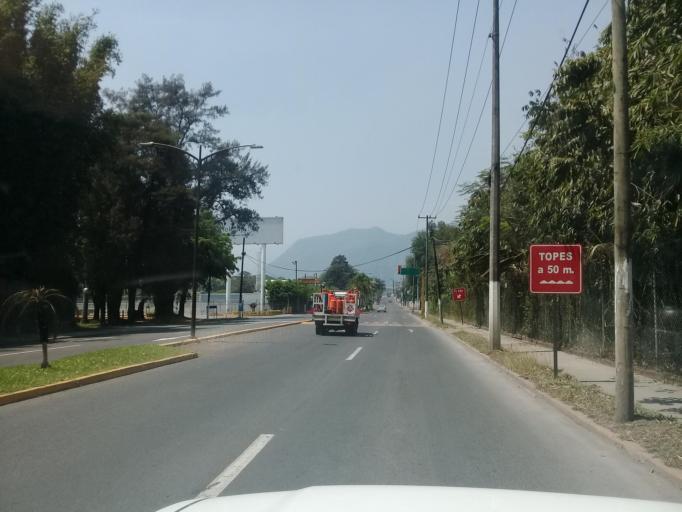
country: MX
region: Veracruz
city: Ixtac Zoquitlan
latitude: 18.8621
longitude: -97.0469
